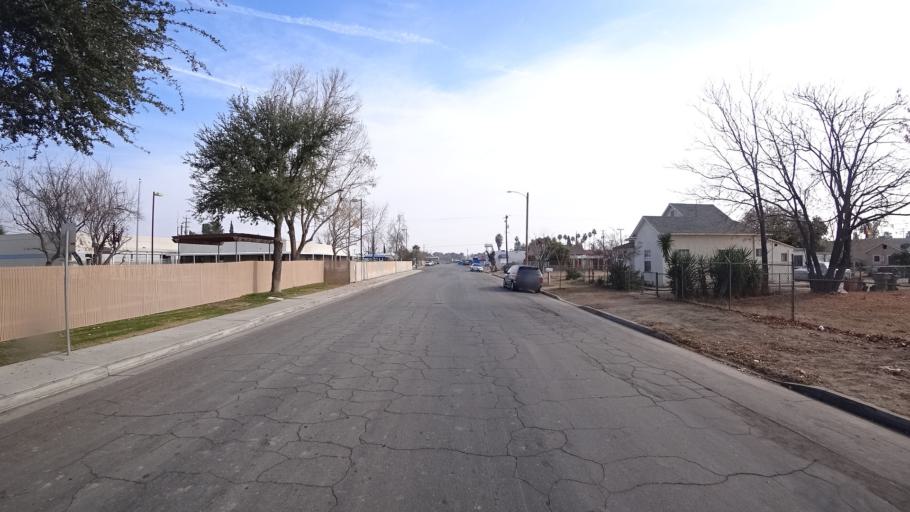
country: US
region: California
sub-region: Kern County
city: Bakersfield
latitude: 35.3695
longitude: -119.0000
